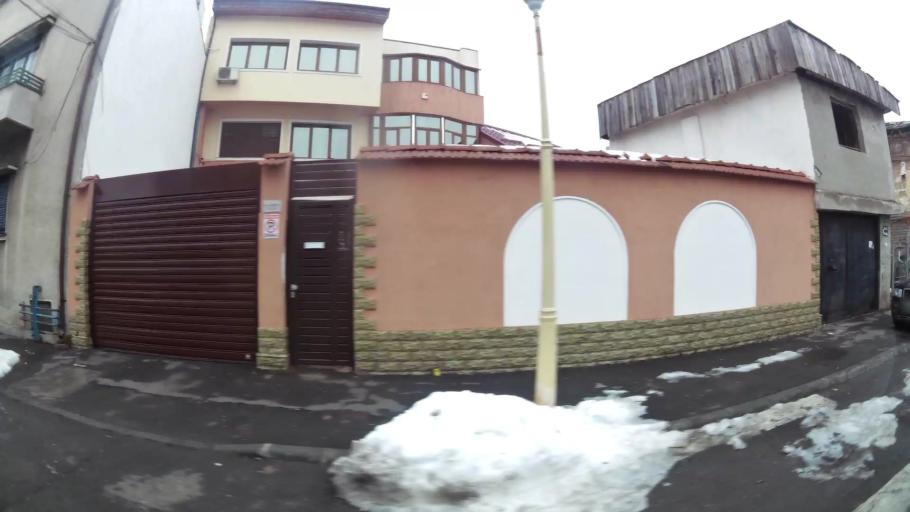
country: RO
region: Bucuresti
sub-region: Municipiul Bucuresti
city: Bucharest
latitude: 44.4361
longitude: 26.1271
